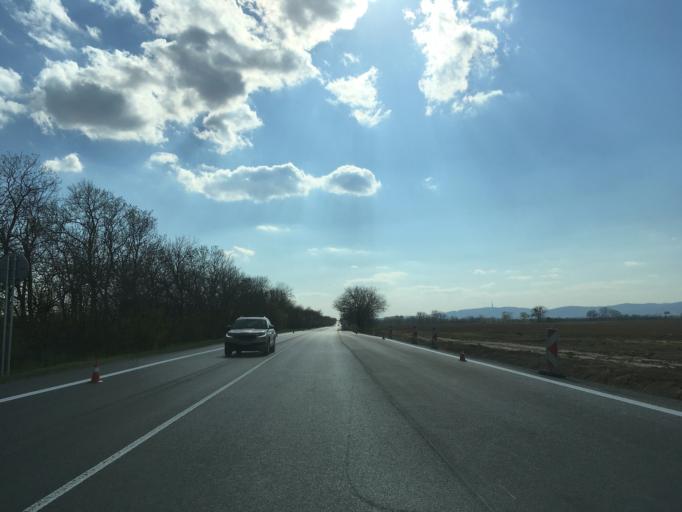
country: SK
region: Bratislavsky
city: Svaty Jur
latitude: 48.2023
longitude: 17.2663
